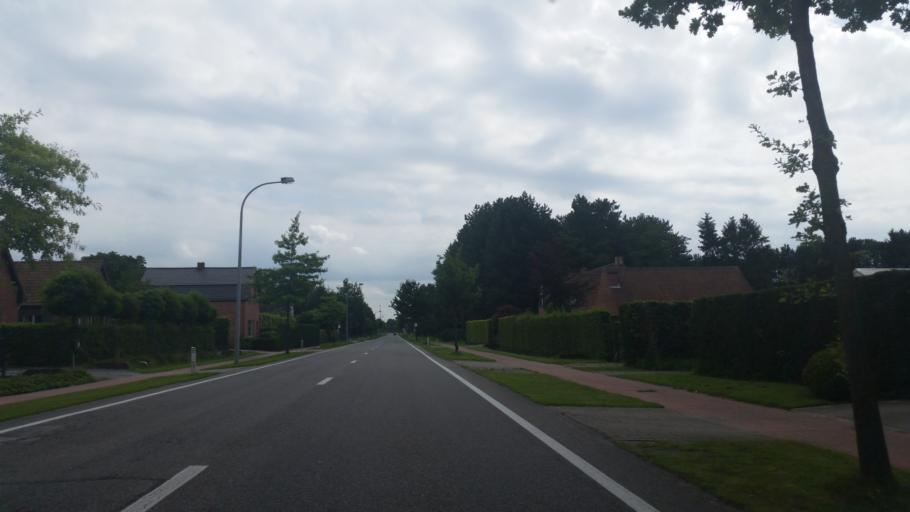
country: BE
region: Flanders
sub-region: Provincie Antwerpen
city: Merksplas
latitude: 51.3832
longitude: 4.8257
